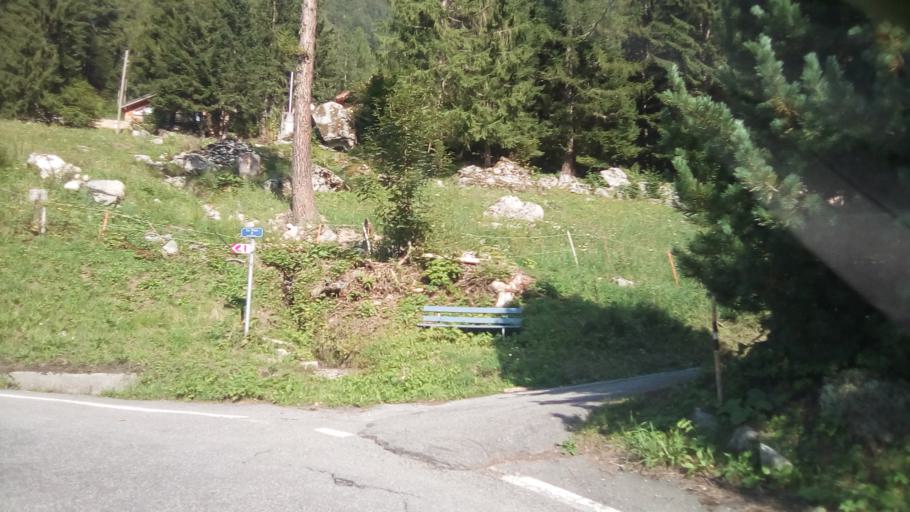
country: CH
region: Valais
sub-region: Martigny District
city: Martigny-Combe
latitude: 46.0527
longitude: 7.0835
